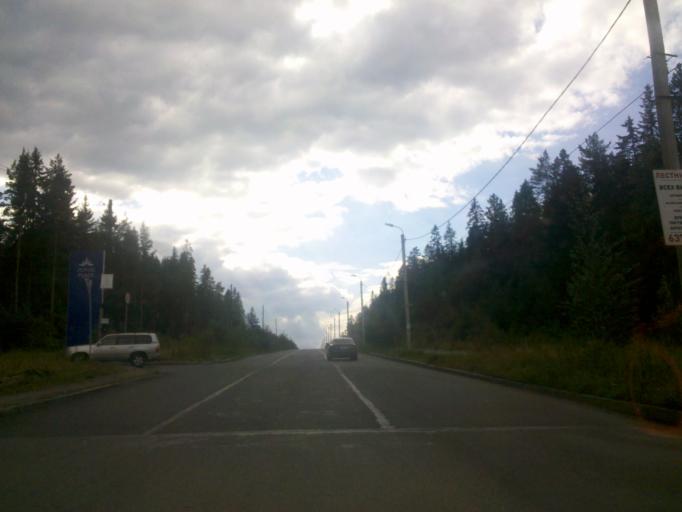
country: RU
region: Republic of Karelia
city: Petrozavodsk
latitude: 61.7779
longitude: 34.3060
